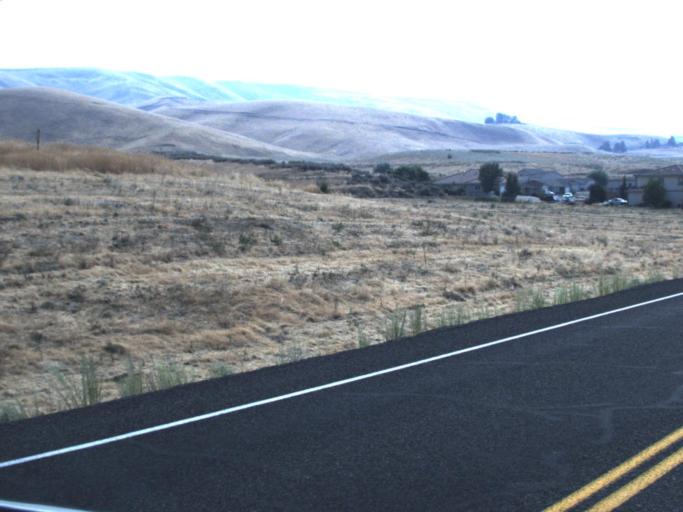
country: US
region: Washington
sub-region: Benton County
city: Prosser
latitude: 46.1950
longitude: -119.7895
